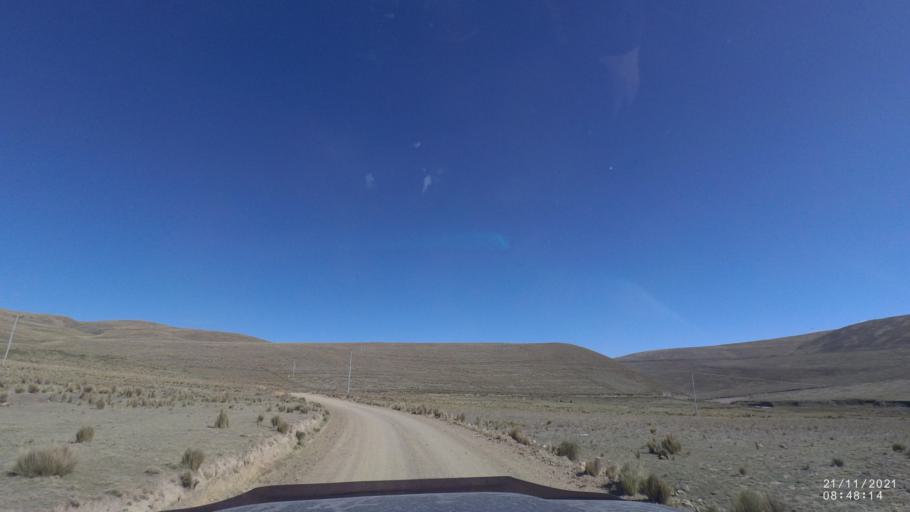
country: BO
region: Cochabamba
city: Cochabamba
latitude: -17.2310
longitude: -66.2332
